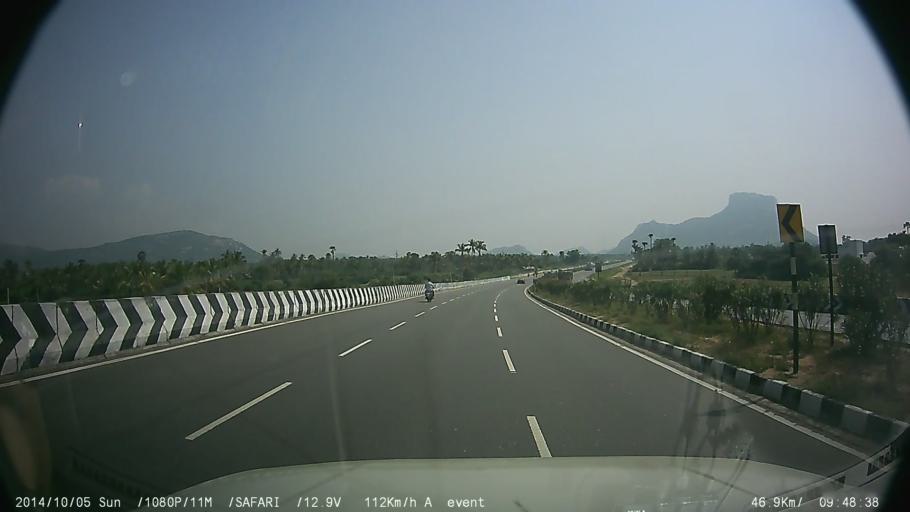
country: IN
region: Tamil Nadu
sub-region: Namakkal
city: Tiruchengode
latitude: 11.4689
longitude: 77.8239
